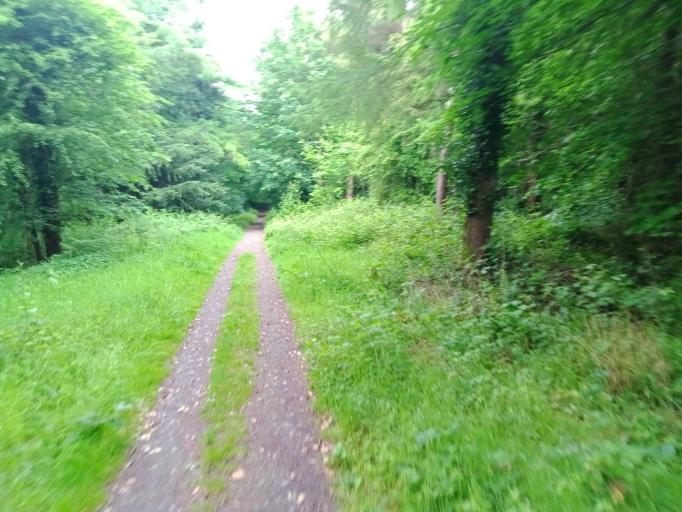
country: IE
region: Leinster
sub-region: Laois
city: Stradbally
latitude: 53.0028
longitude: -7.1230
